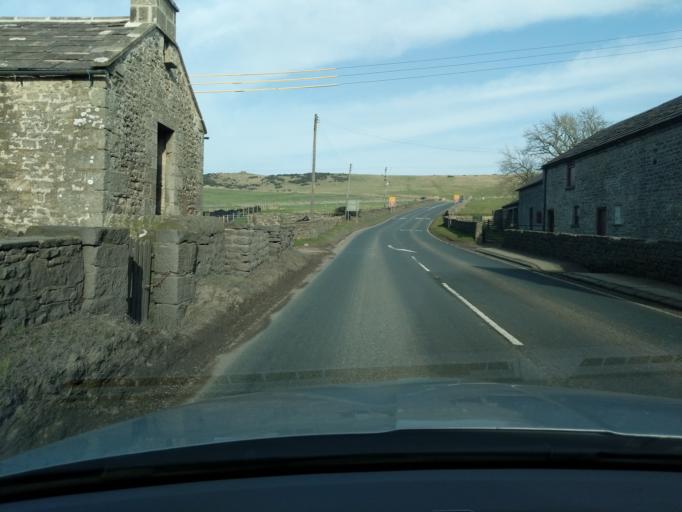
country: GB
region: England
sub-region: North Yorkshire
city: Leyburn
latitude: 54.3505
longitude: -1.8064
